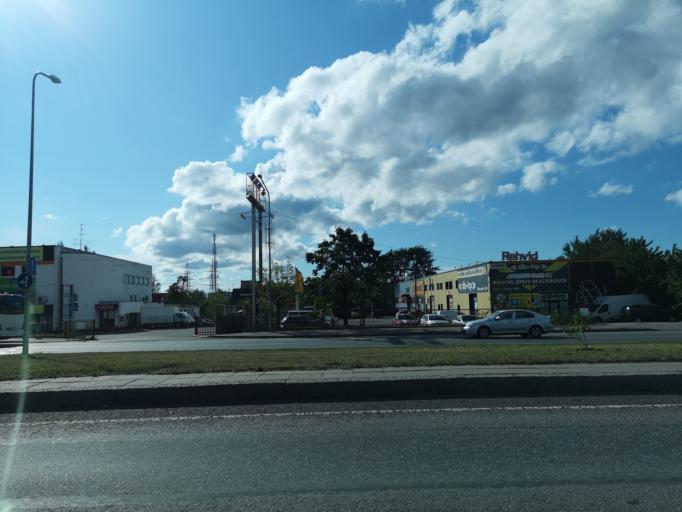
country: EE
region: Harju
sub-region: Tallinna linn
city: Tallinn
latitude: 59.3982
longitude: 24.7269
